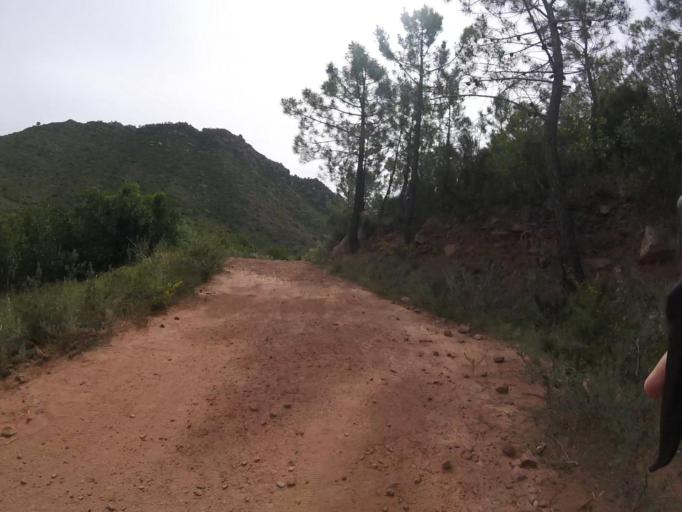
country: ES
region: Valencia
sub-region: Provincia de Castello
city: Benicassim
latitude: 40.0694
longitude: 0.0384
